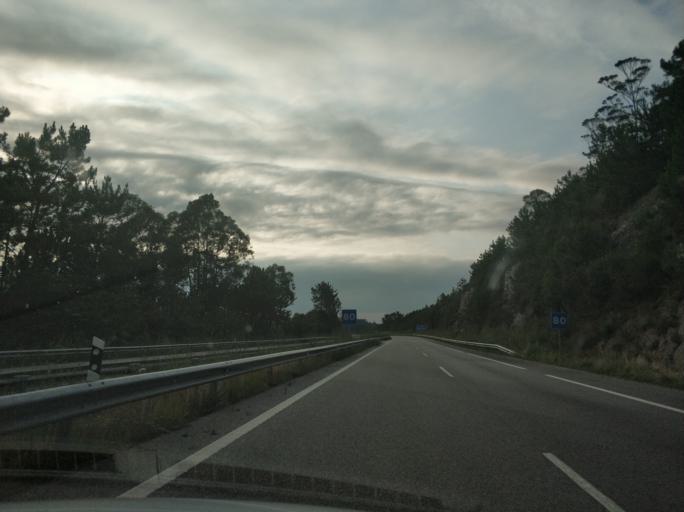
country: ES
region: Asturias
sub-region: Province of Asturias
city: Cudillero
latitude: 43.5648
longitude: -6.2145
